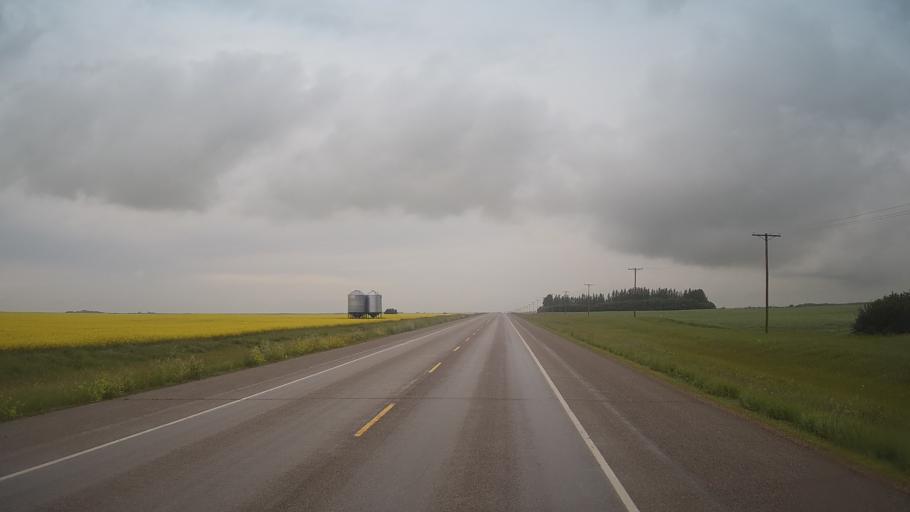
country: CA
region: Saskatchewan
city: Wilkie
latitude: 52.4055
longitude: -108.7873
